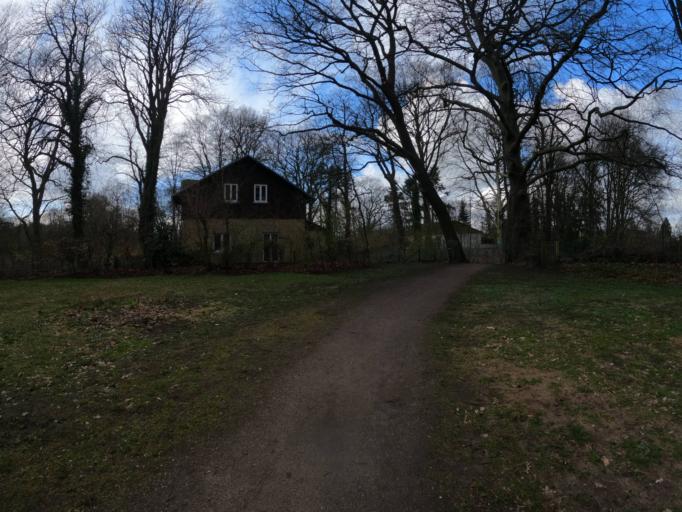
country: DE
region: Hamburg
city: Stellingen
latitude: 53.6020
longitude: 9.9477
